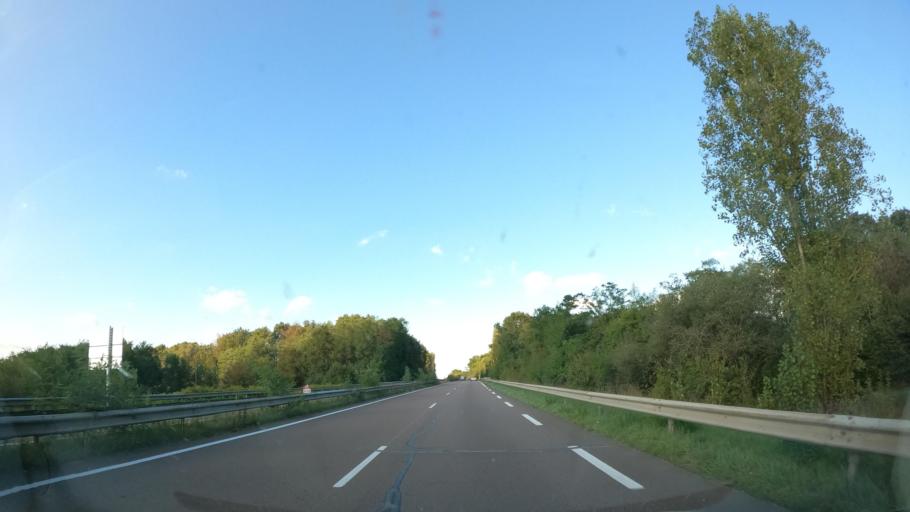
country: FR
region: Bourgogne
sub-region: Departement de Saone-et-Loire
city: Sanvignes-les-Mines
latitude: 46.6521
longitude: 4.3296
